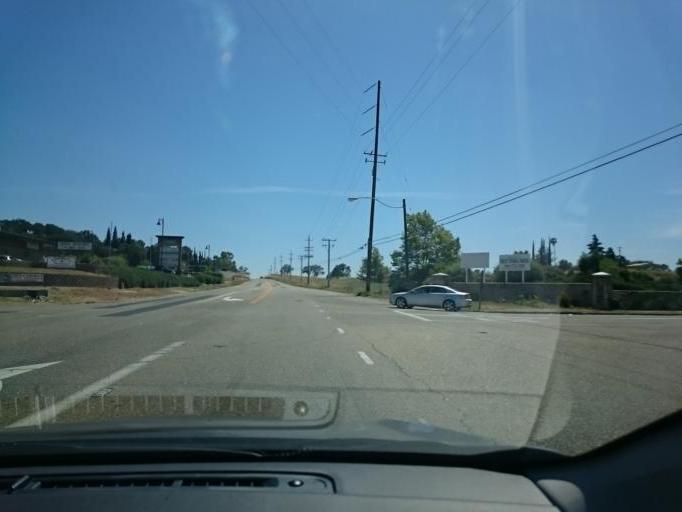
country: US
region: California
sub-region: Calaveras County
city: Valley Springs
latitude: 38.1689
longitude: -120.8390
